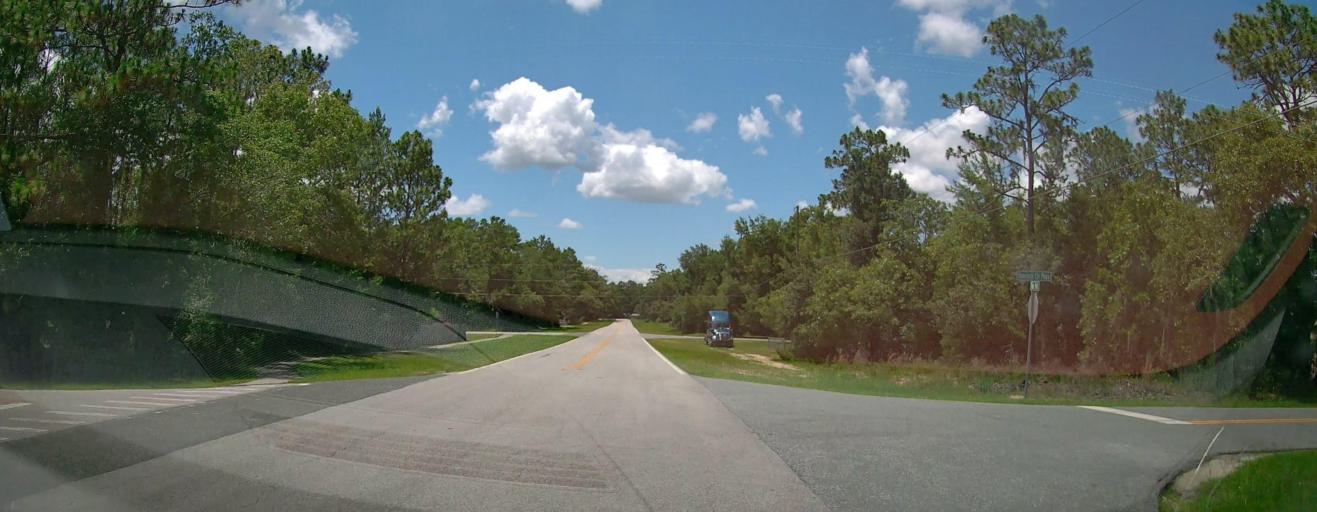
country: US
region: Florida
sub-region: Marion County
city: Silver Springs Shores
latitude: 29.1407
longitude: -82.0311
